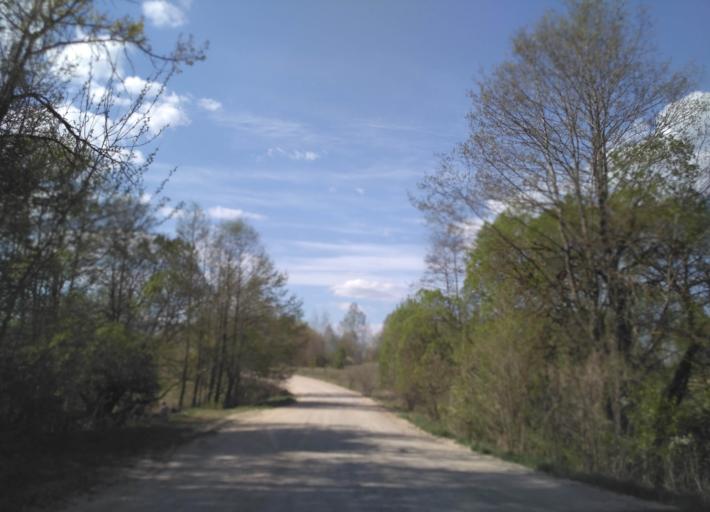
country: BY
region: Minsk
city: Narach
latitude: 54.9829
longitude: 26.6164
